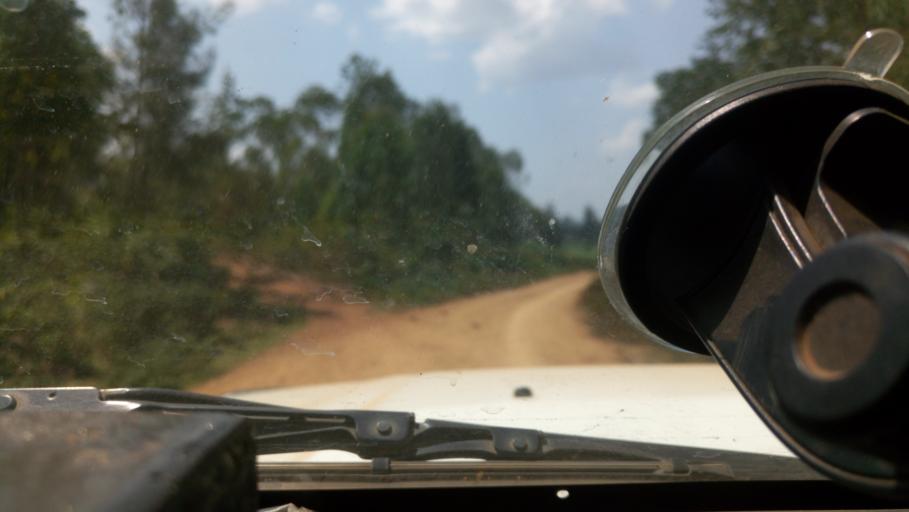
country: KE
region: Migori
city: Migori
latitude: -0.9417
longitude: 34.4453
